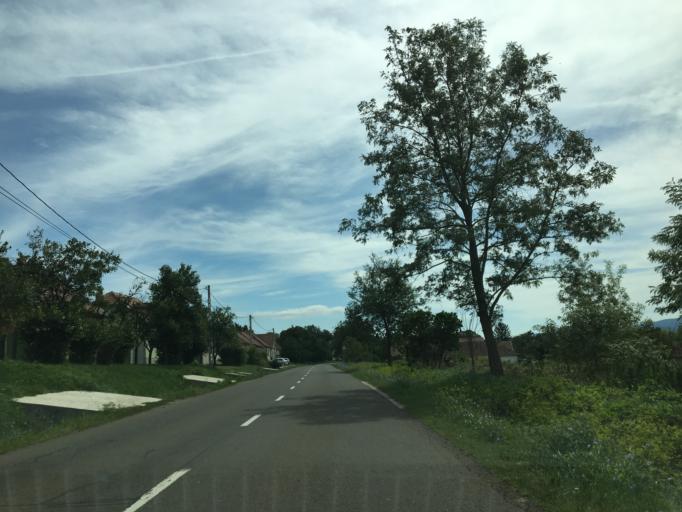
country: HU
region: Pest
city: Szob
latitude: 47.8447
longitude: 18.8246
